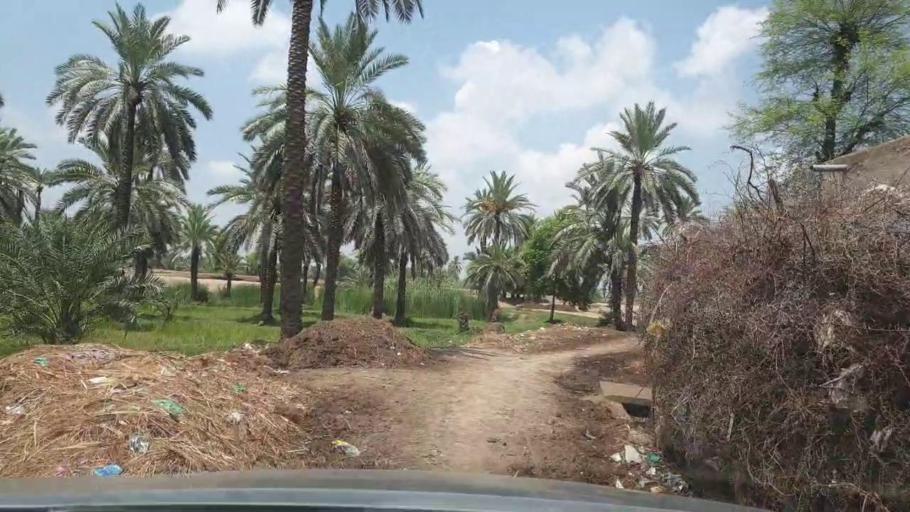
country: PK
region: Sindh
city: Pir jo Goth
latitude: 27.6126
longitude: 68.6039
